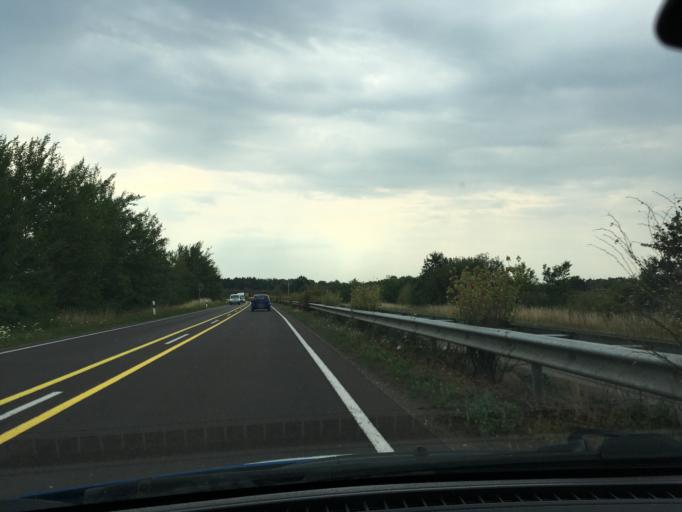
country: DE
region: Lower Saxony
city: Burgdorf
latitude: 52.4666
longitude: 9.9613
